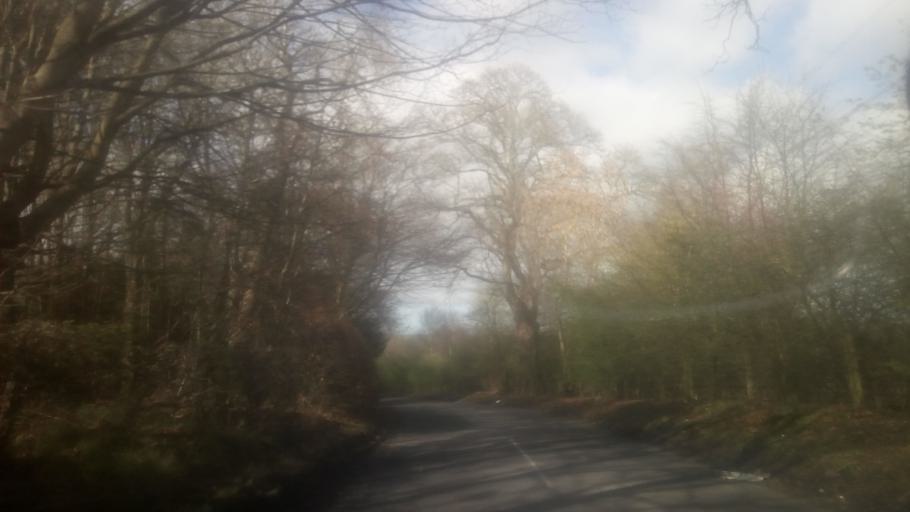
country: GB
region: Scotland
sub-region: East Lothian
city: Ormiston
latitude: 55.8936
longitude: -2.9549
